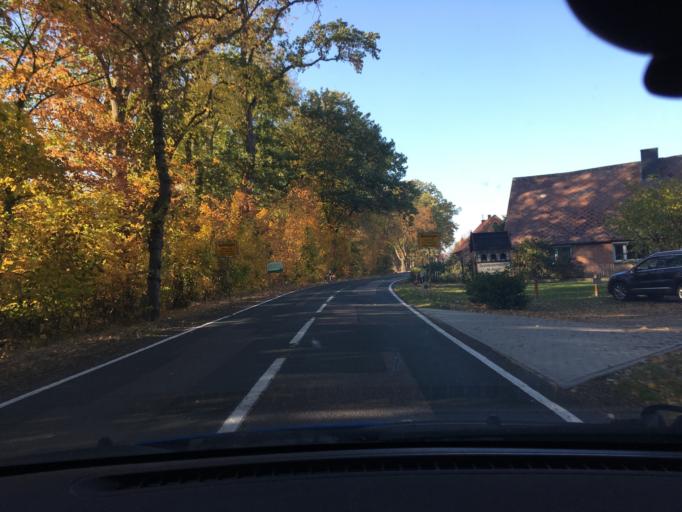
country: DE
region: Lower Saxony
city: Damnatz
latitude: 53.1683
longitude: 11.1705
